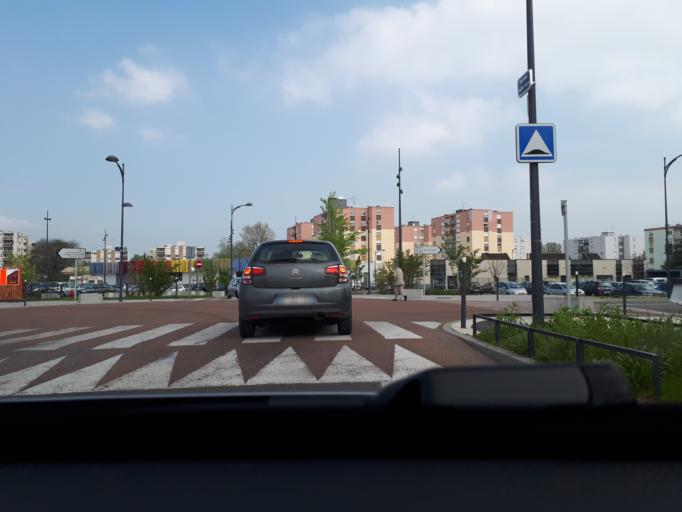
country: FR
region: Rhone-Alpes
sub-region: Departement de l'Isere
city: Bourgoin-Jallieu
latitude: 45.6064
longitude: 5.2661
